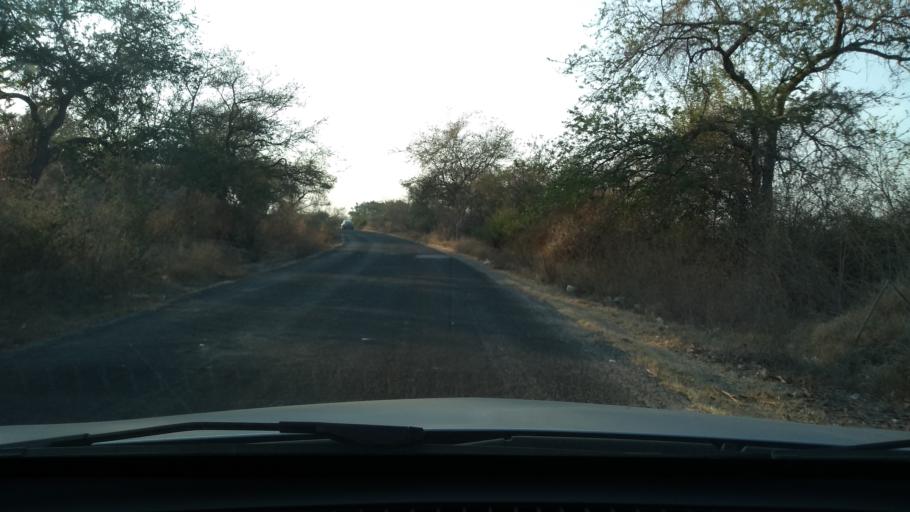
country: MX
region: Morelos
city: Puente de Ixtla
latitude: 18.6001
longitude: -99.3078
